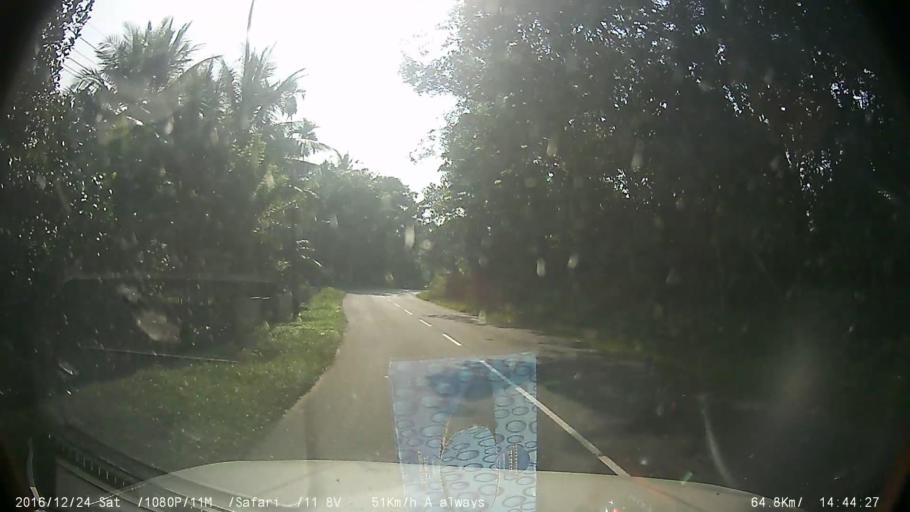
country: IN
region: Kerala
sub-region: Kottayam
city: Lalam
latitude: 9.7767
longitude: 76.7200
